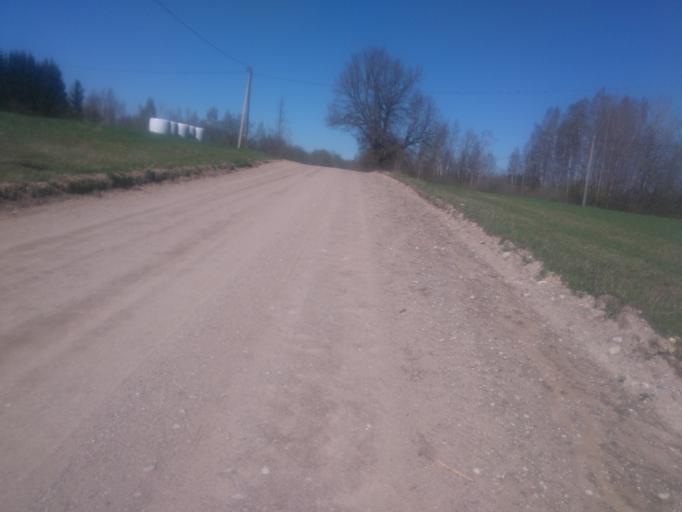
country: LV
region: Vecpiebalga
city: Vecpiebalga
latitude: 57.0256
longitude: 25.8400
